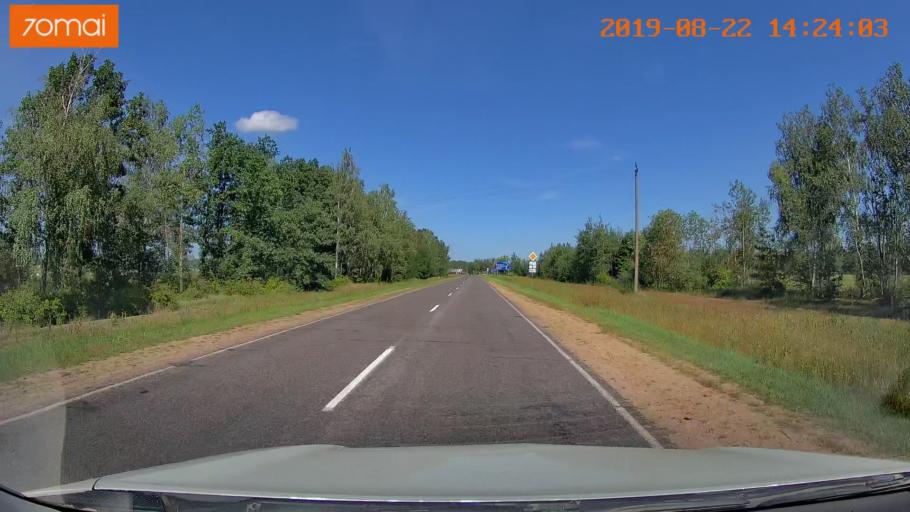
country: BY
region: Mogilev
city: Asipovichy
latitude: 53.2956
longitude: 28.5934
